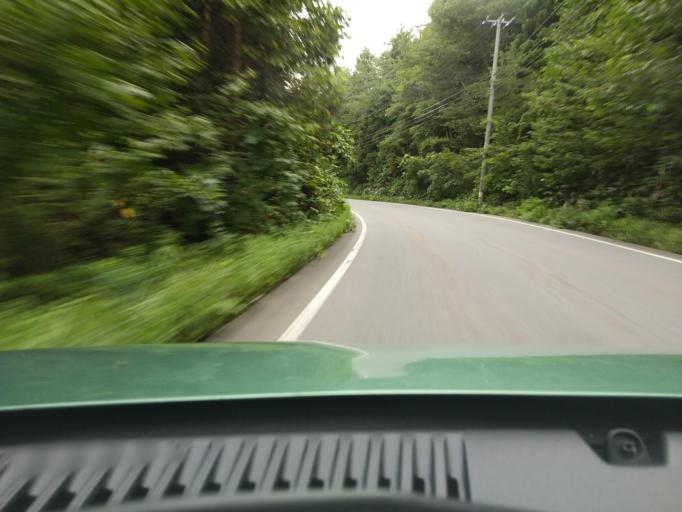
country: JP
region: Akita
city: Akita
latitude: 39.7744
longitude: 140.1337
